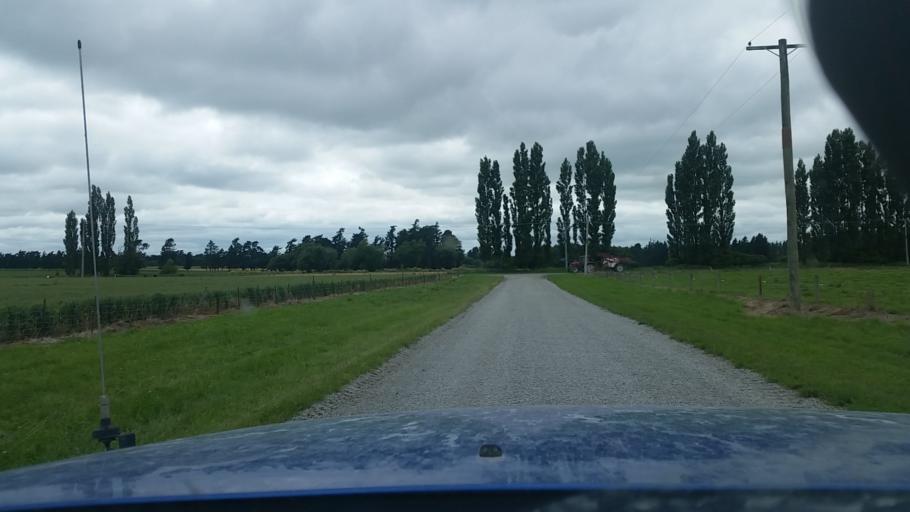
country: NZ
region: Canterbury
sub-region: Ashburton District
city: Methven
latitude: -43.8059
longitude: 171.4145
